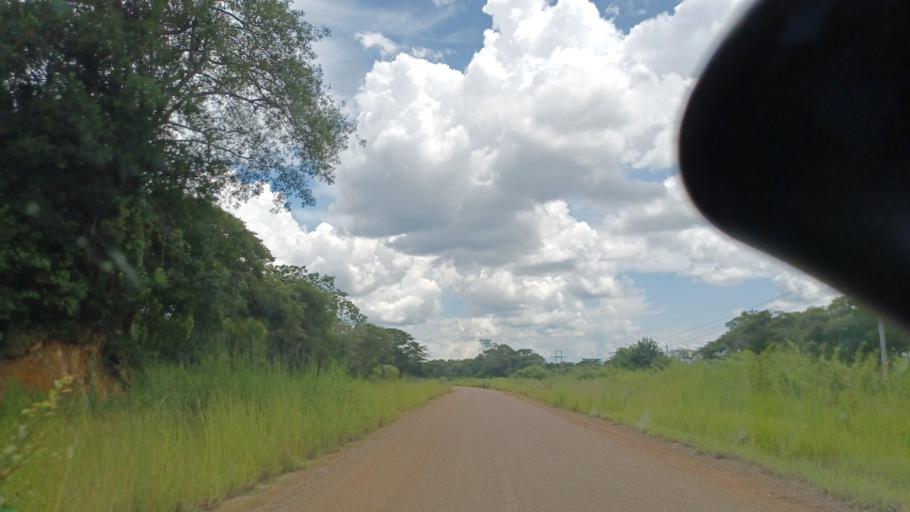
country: ZM
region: North-Western
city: Solwezi
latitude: -12.7154
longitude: 26.0220
